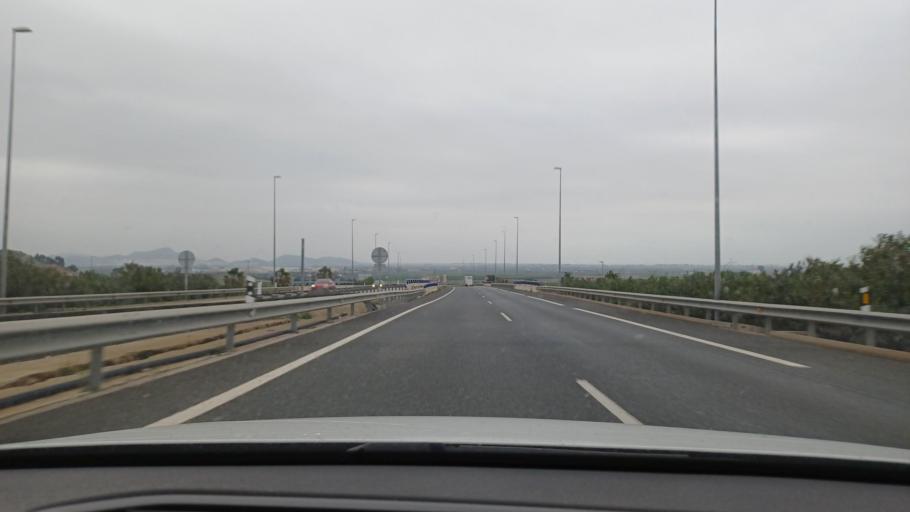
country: ES
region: Valencia
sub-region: Provincia de Valencia
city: Faura
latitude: 39.7035
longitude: -0.2618
